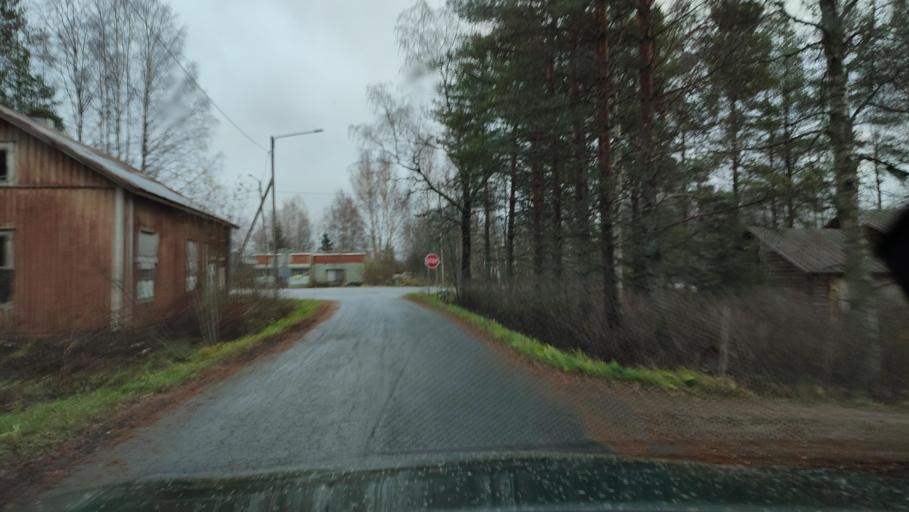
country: FI
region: Southern Ostrobothnia
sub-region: Suupohja
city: Teuva
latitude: 62.4564
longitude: 21.6045
